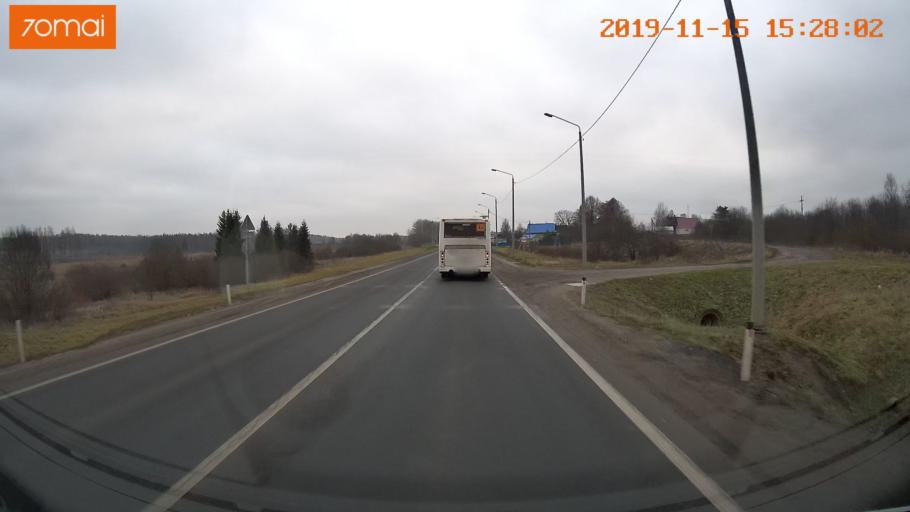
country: RU
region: Jaroslavl
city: Danilov
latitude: 58.1357
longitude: 40.1384
